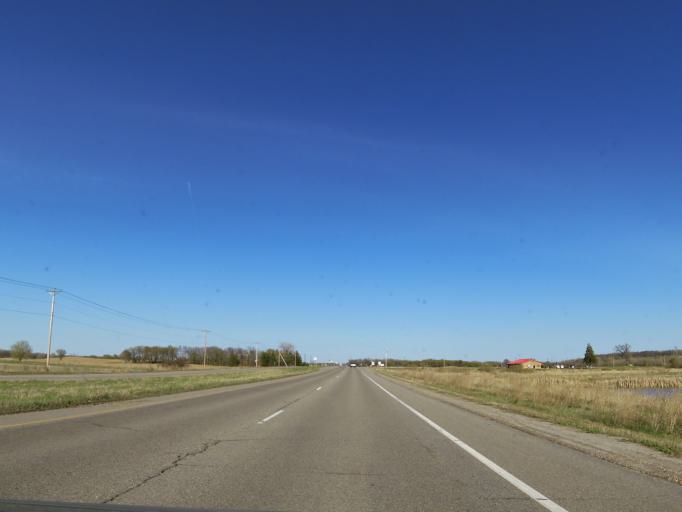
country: US
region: Minnesota
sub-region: Scott County
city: Elko New Market
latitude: 44.5730
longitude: -93.3357
